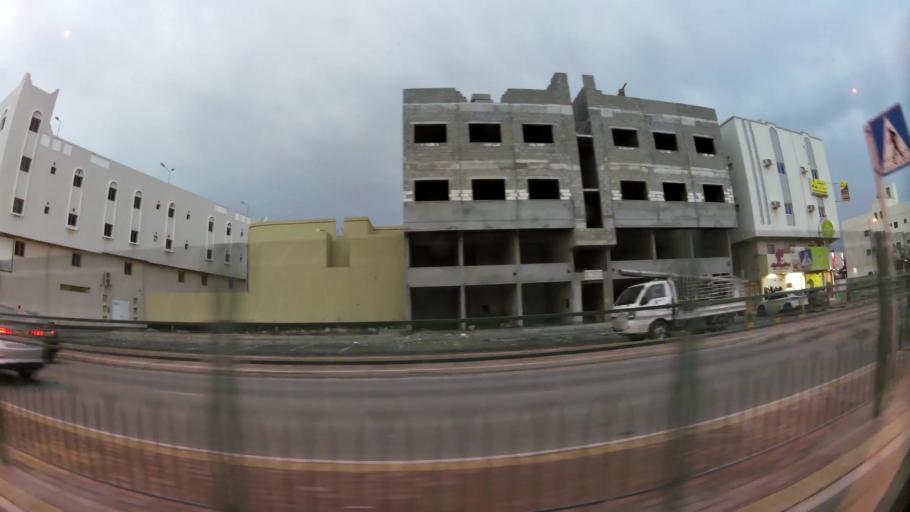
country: BH
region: Central Governorate
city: Madinat Hamad
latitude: 26.1541
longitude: 50.5099
